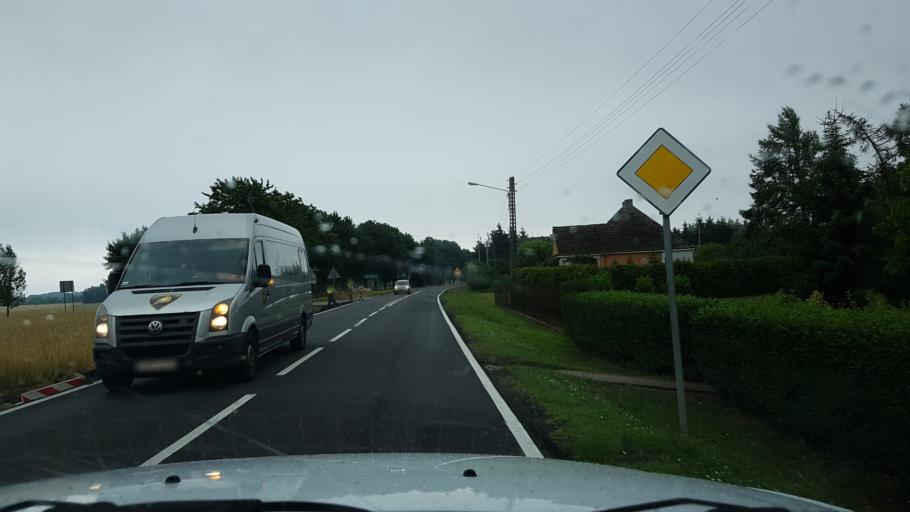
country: PL
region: West Pomeranian Voivodeship
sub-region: Powiat mysliborski
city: Mysliborz
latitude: 52.9343
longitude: 14.8256
